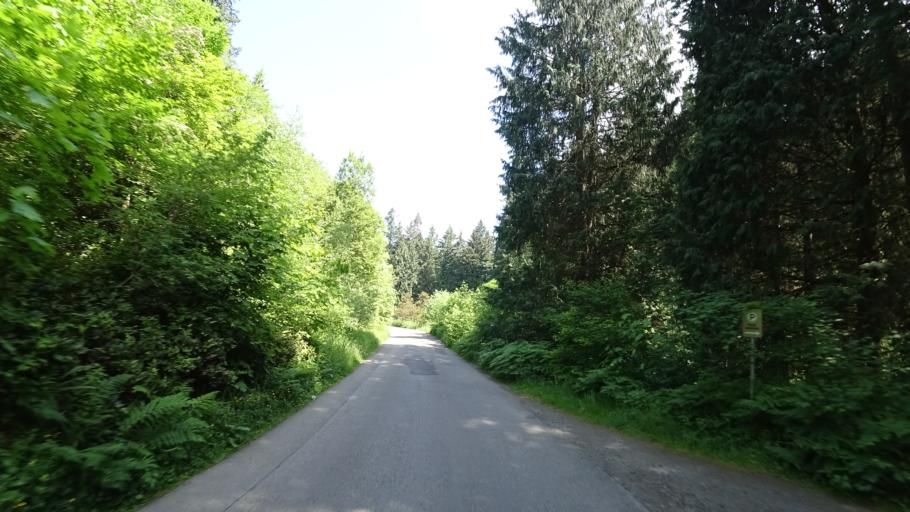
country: US
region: Oregon
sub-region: Multnomah County
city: Portland
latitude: 45.5179
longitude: -122.7180
